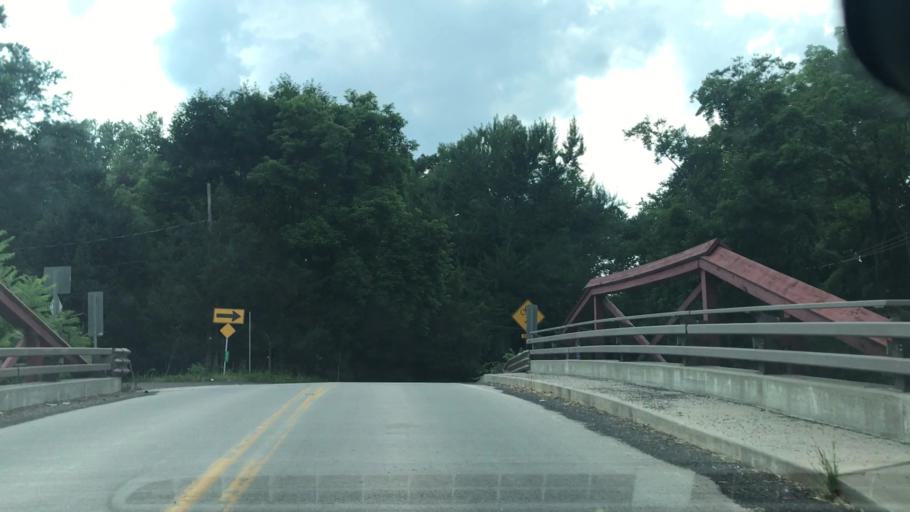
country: US
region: Pennsylvania
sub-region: Bucks County
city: New Hope
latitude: 40.3752
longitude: -74.9562
